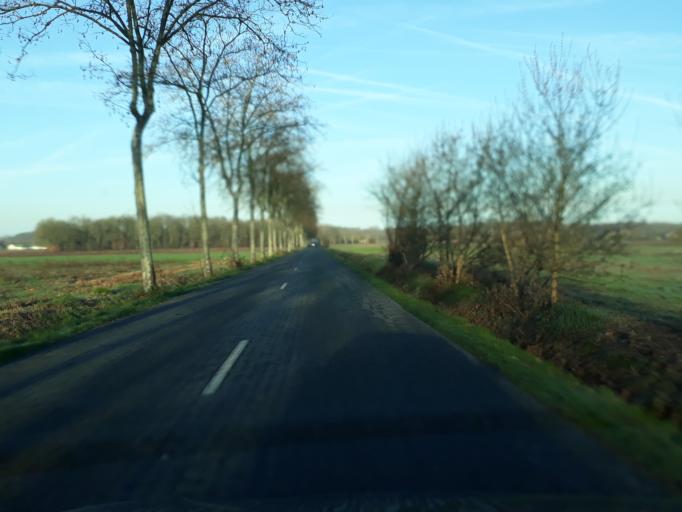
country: FR
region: Midi-Pyrenees
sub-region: Departement de la Haute-Garonne
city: Rieumes
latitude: 43.4249
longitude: 1.1430
